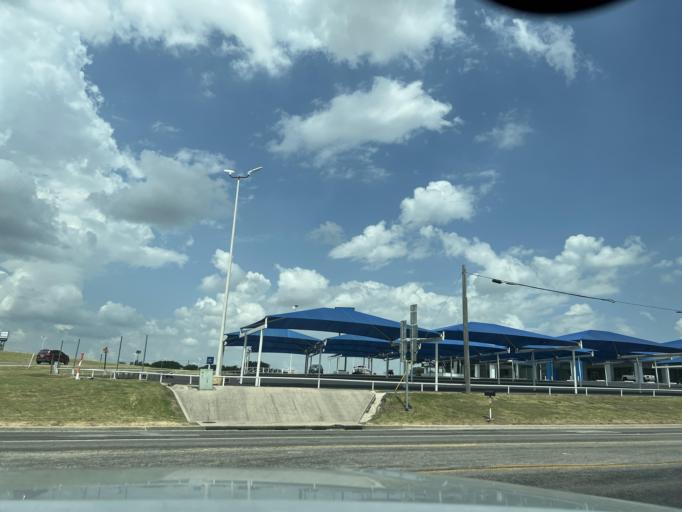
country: US
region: Texas
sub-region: Wise County
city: Decatur
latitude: 33.2154
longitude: -97.5833
